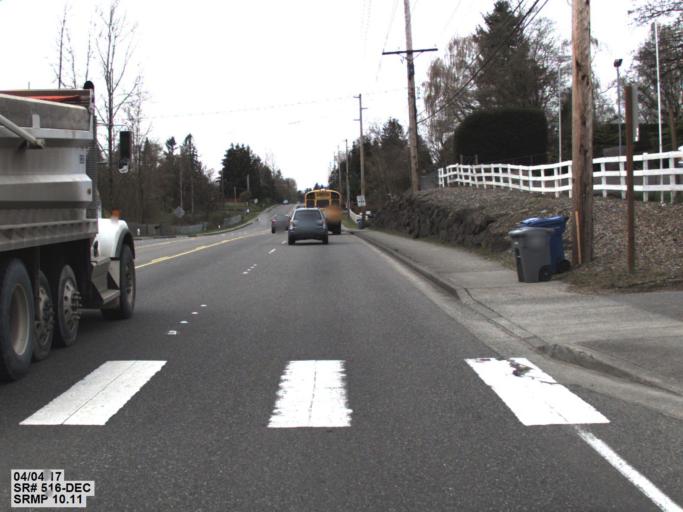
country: US
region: Washington
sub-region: King County
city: Covington
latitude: 47.3580
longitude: -122.1497
